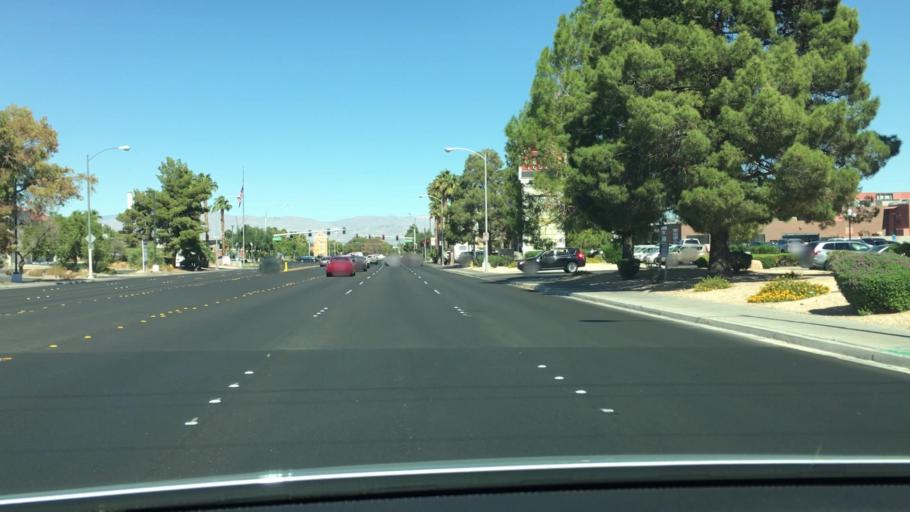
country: US
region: Nevada
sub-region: Clark County
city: Winchester
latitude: 36.1134
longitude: -115.1008
